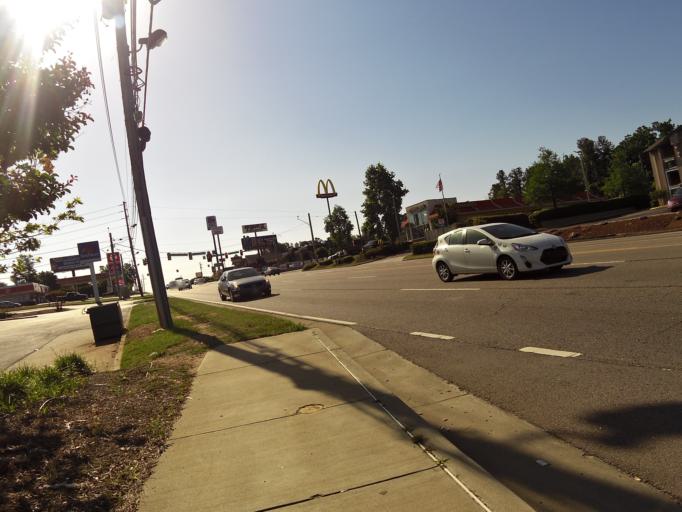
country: US
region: Georgia
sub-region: Columbia County
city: Martinez
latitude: 33.5117
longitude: -82.0392
